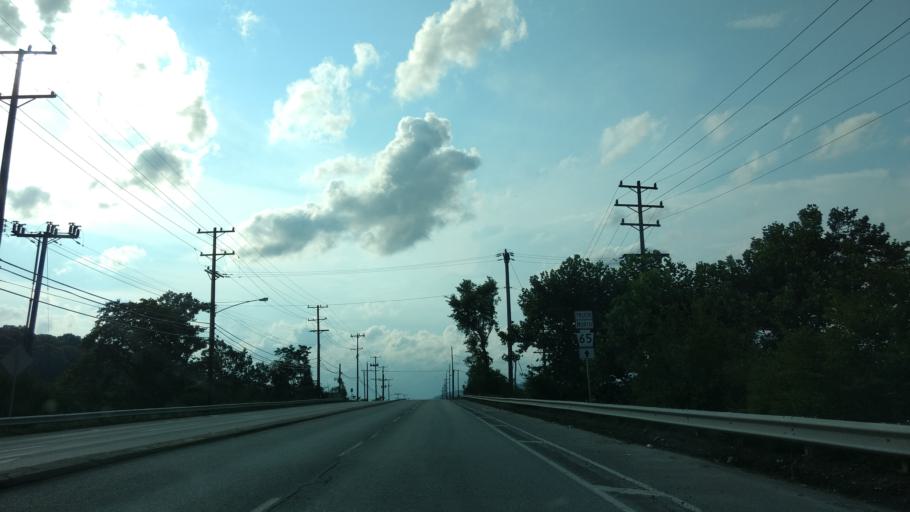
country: US
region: Pennsylvania
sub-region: Allegheny County
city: Ben Avon
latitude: 40.4931
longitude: -80.0812
